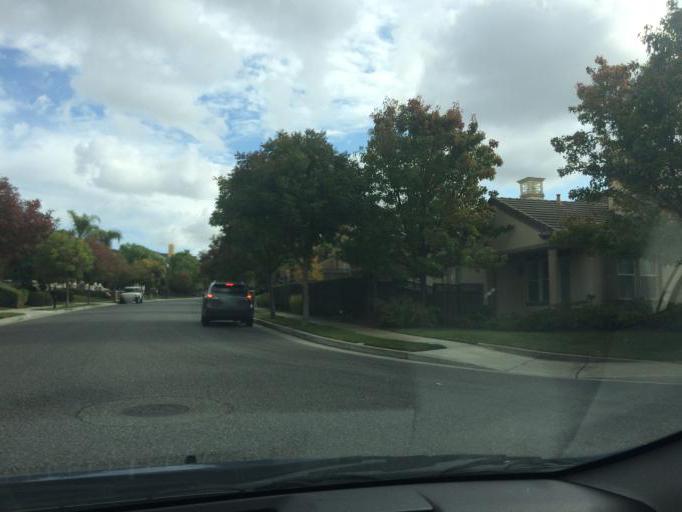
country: US
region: California
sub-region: Santa Clara County
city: Seven Trees
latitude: 37.2876
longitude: -121.7943
